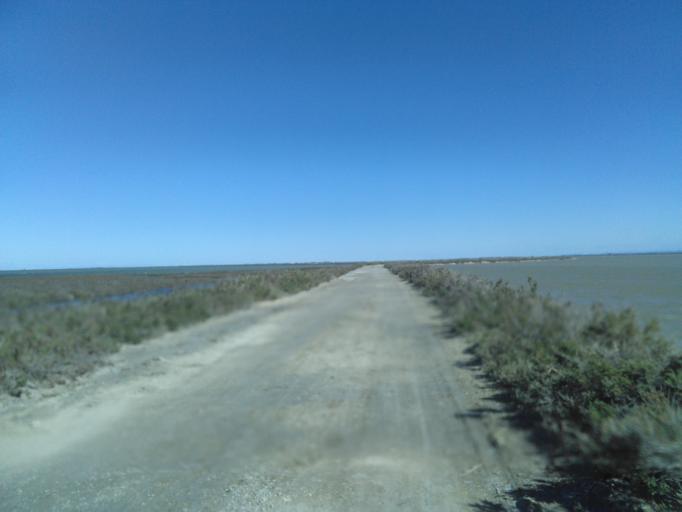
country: FR
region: Provence-Alpes-Cote d'Azur
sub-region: Departement des Bouches-du-Rhone
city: Saintes-Maries-de-la-Mer
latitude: 43.4246
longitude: 4.6187
